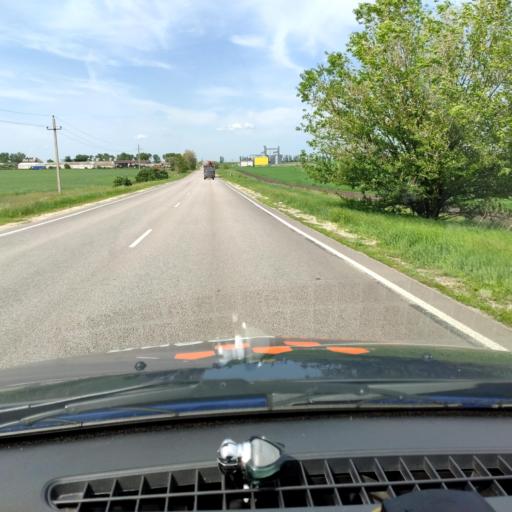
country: RU
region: Voronezj
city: Novaya Usman'
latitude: 51.5746
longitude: 39.3752
